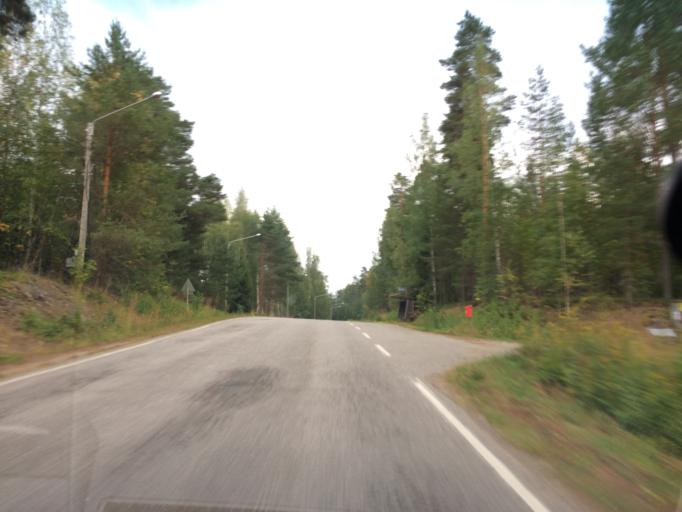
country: FI
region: Pirkanmaa
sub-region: Tampere
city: Luopioinen
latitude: 61.2522
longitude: 24.7063
